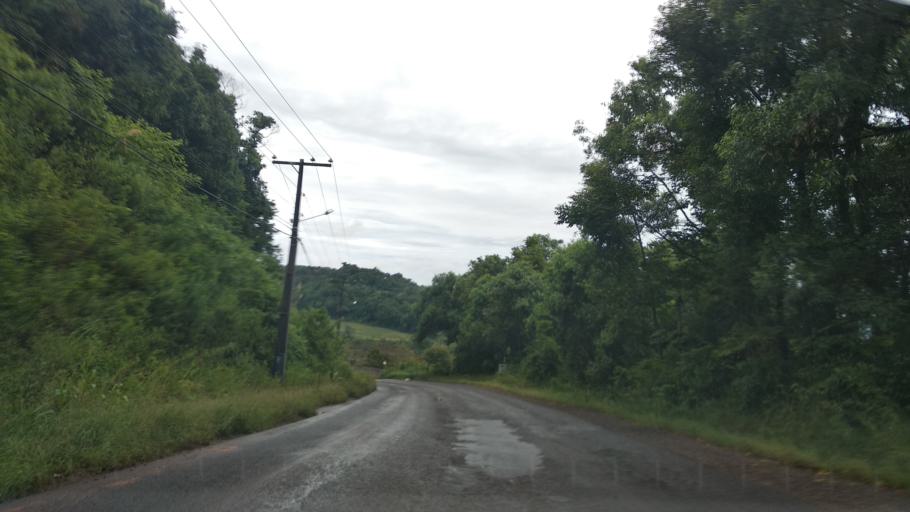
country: BR
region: Santa Catarina
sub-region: Videira
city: Videira
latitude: -27.0000
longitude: -51.1768
